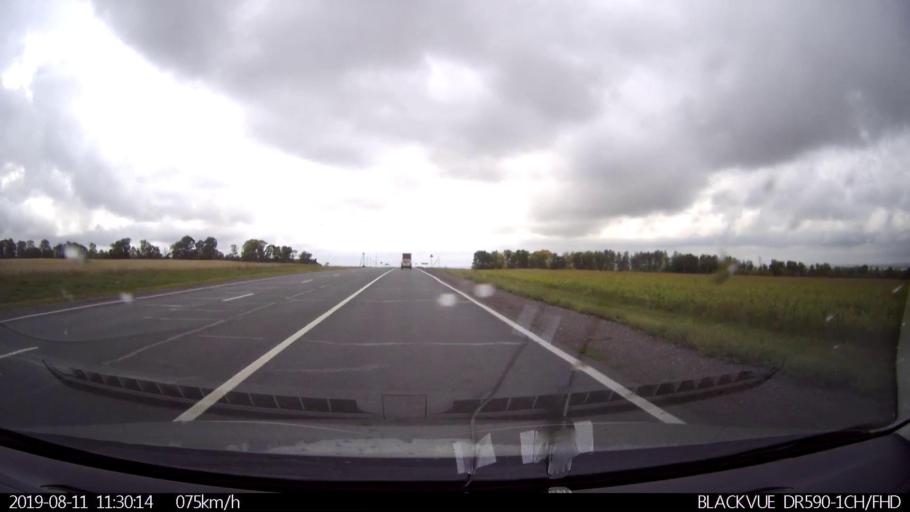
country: RU
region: Ulyanovsk
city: Krasnyy Gulyay
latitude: 54.0611
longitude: 48.2202
